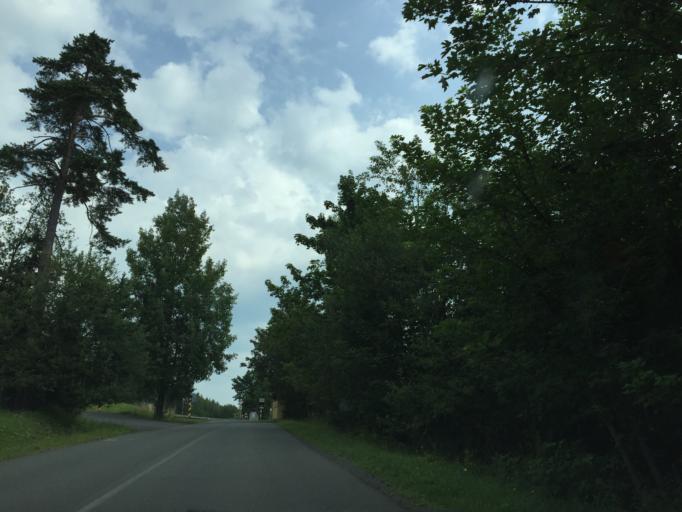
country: SK
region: Presovsky
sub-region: Okres Poprad
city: Vysoke Tatry
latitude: 49.1419
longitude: 20.2406
